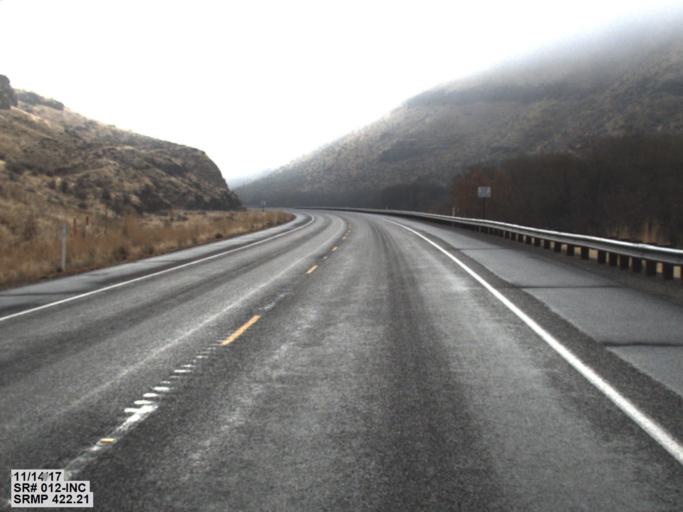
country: US
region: Washington
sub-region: Asotin County
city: Clarkston Heights-Vineland
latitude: 46.4093
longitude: -117.2658
